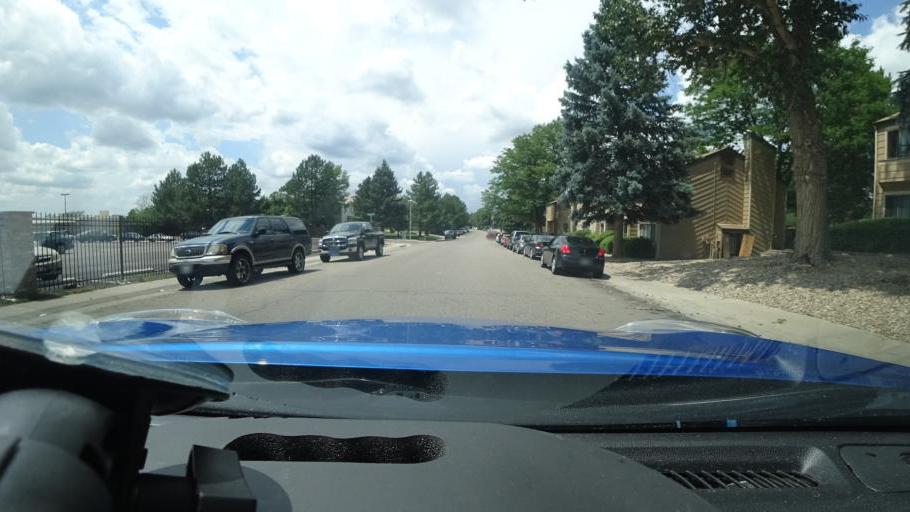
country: US
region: Colorado
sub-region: Adams County
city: Aurora
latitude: 39.6990
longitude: -104.8418
